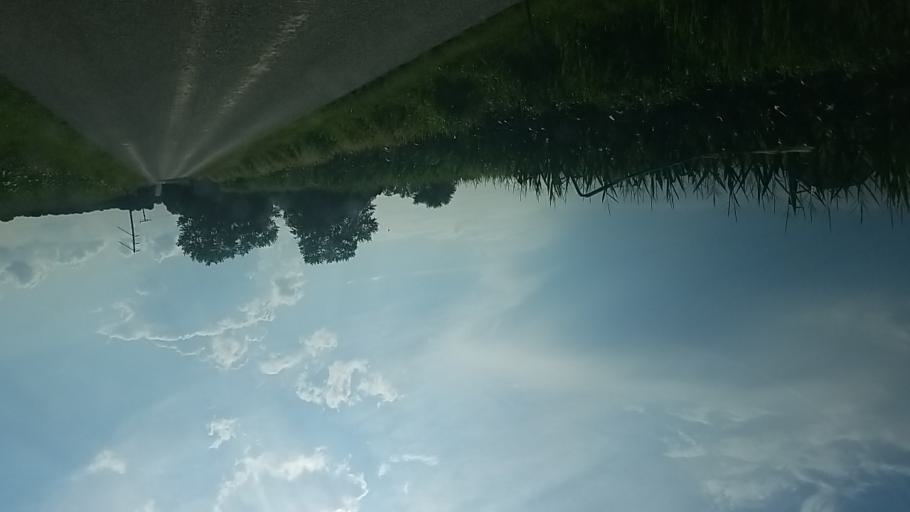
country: US
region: Ohio
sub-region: Wayne County
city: Smithville
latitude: 40.8651
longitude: -81.9050
